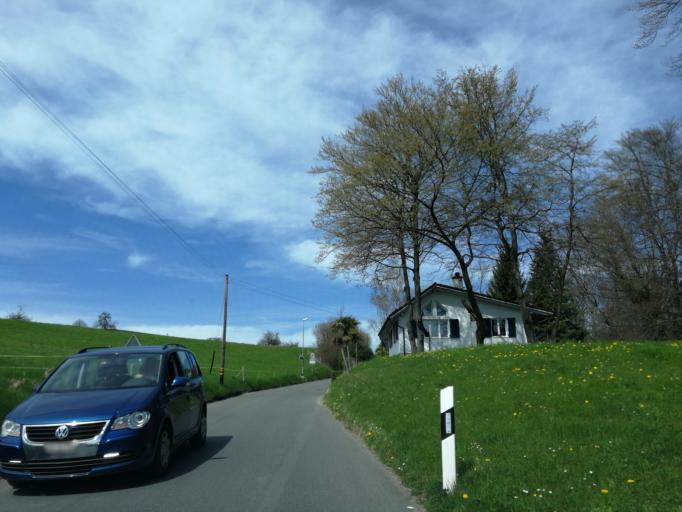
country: CH
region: Zurich
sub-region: Bezirk Meilen
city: Meilen
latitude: 47.2763
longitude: 8.6381
